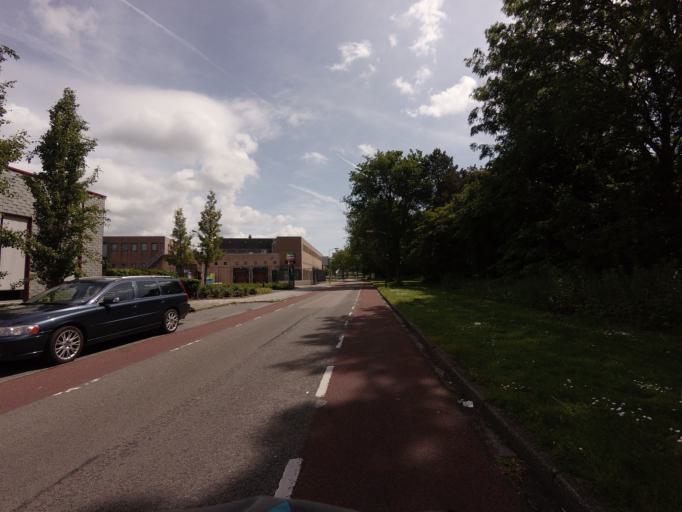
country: NL
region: North Holland
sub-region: Gemeente Hoorn
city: Hoorn
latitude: 52.6449
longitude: 5.0421
